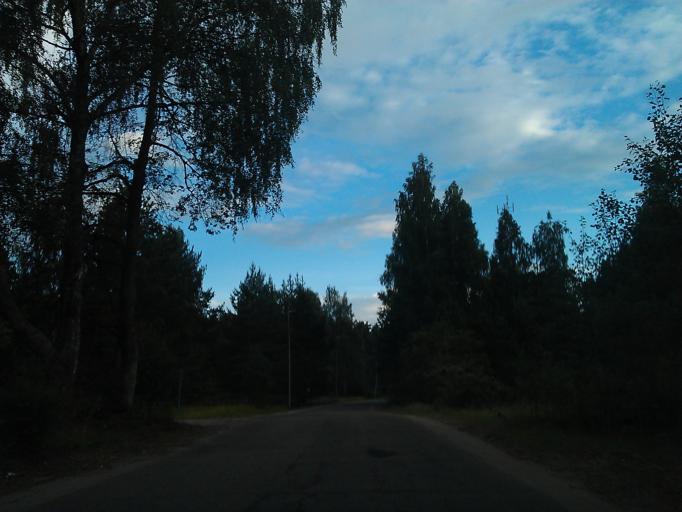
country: LV
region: Carnikava
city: Carnikava
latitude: 57.1859
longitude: 24.3426
